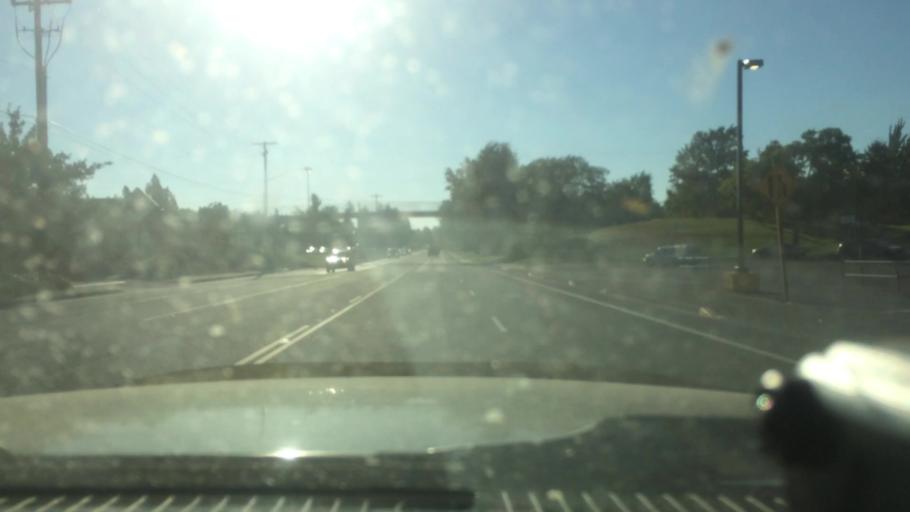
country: US
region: Oregon
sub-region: Lane County
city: Eugene
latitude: 44.0404
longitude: -123.1171
